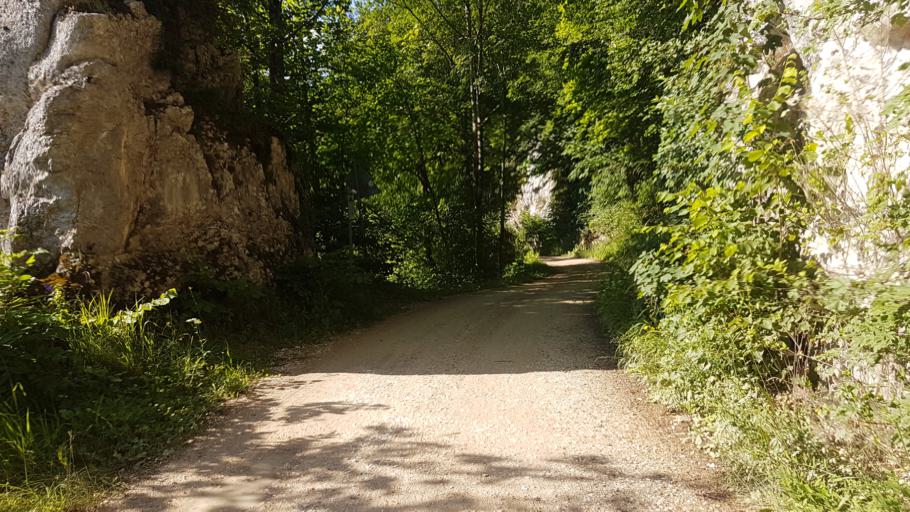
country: DE
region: Baden-Wuerttemberg
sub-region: Tuebingen Region
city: Stetten am Kalten Markt
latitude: 48.0873
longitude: 9.1013
